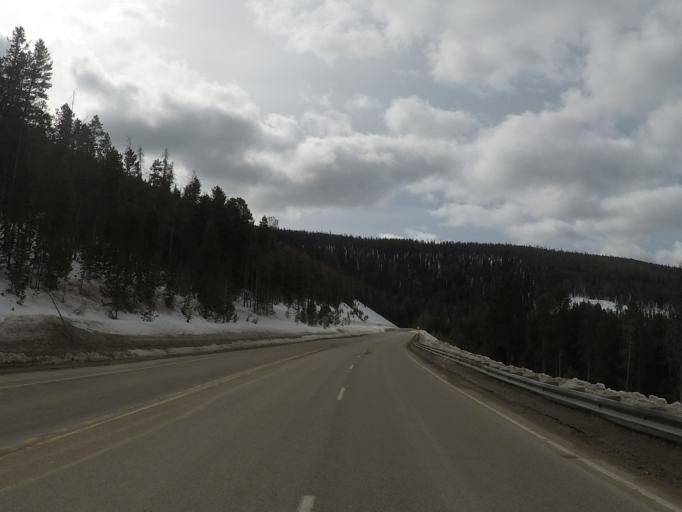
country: US
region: Idaho
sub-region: Lemhi County
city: Salmon
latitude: 45.7098
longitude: -113.9348
